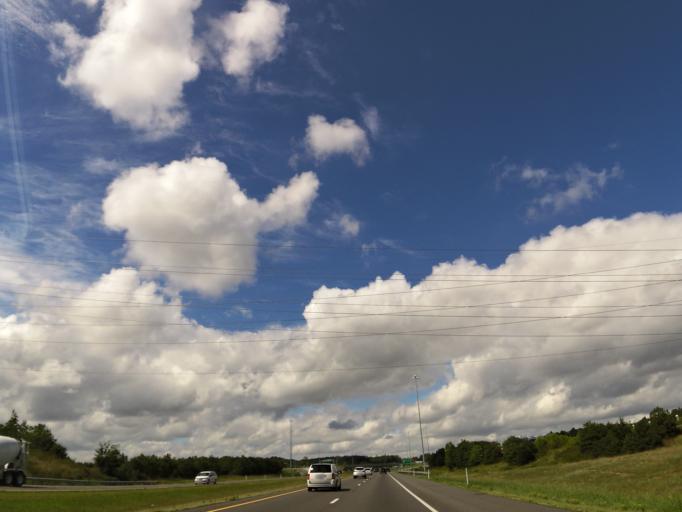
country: US
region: Tennessee
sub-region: Bradley County
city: Cleveland
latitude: 35.1563
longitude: -84.9415
